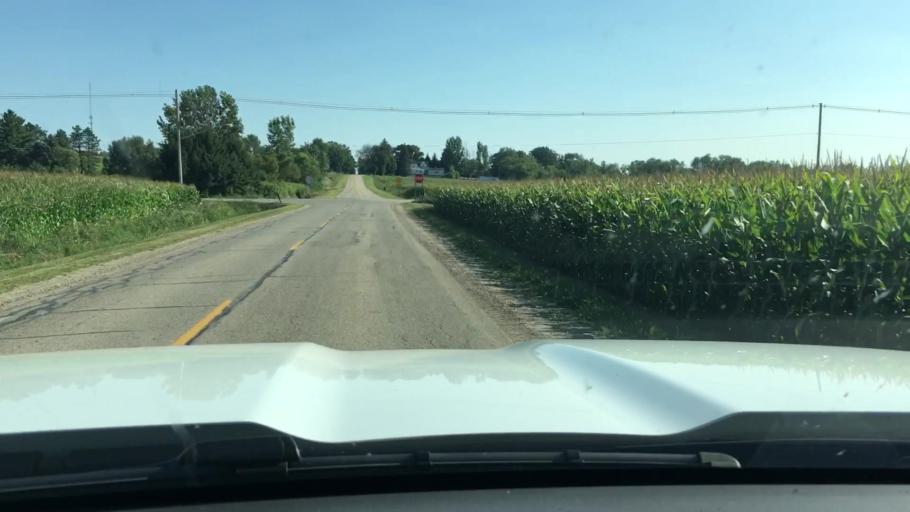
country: US
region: Michigan
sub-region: Ottawa County
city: Zeeland
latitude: 42.8275
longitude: -85.9598
